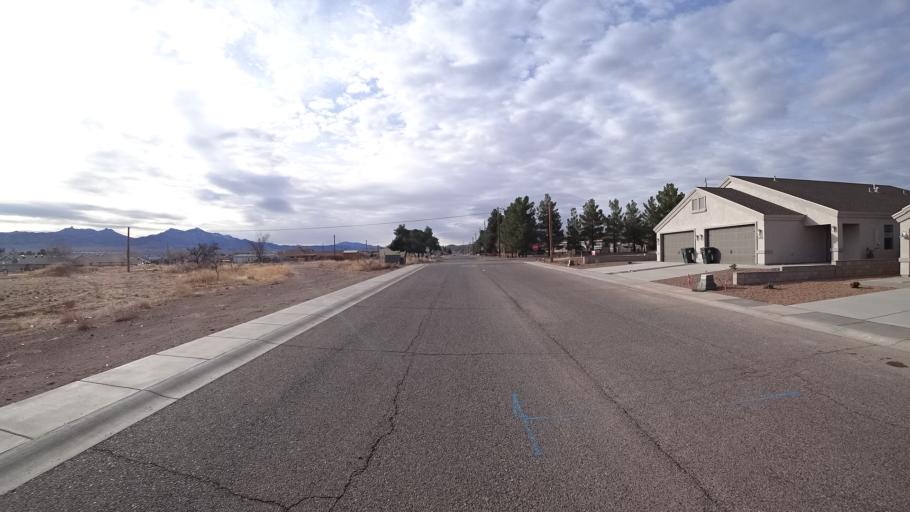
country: US
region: Arizona
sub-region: Mohave County
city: Kingman
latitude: 35.2226
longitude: -114.0446
